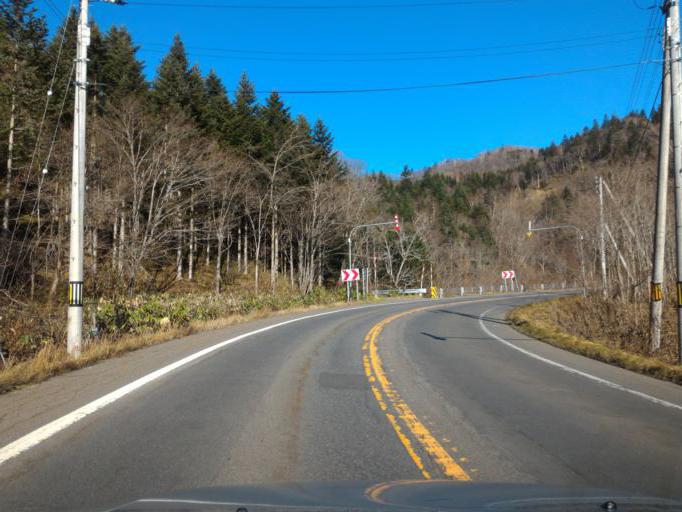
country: JP
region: Hokkaido
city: Bibai
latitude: 43.2832
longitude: 142.0628
